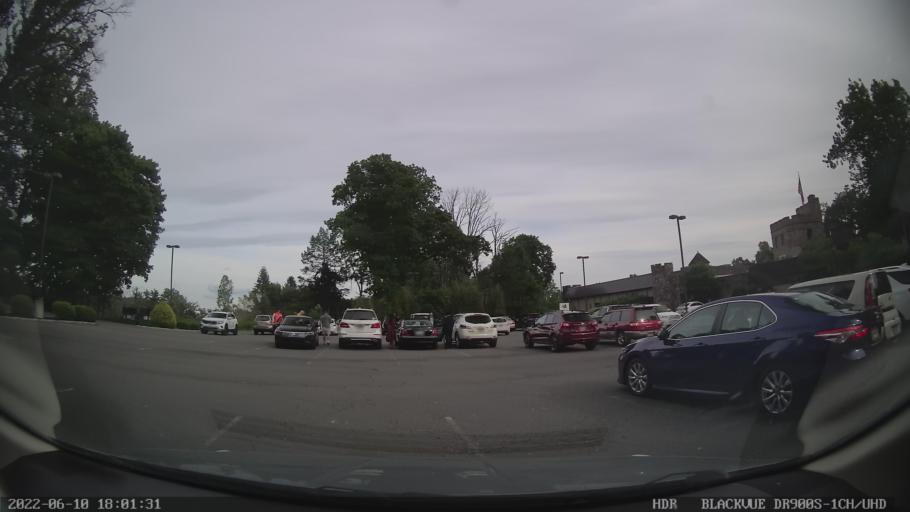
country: US
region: Pennsylvania
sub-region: Berks County
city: Mount Penn
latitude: 40.3372
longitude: -75.8916
